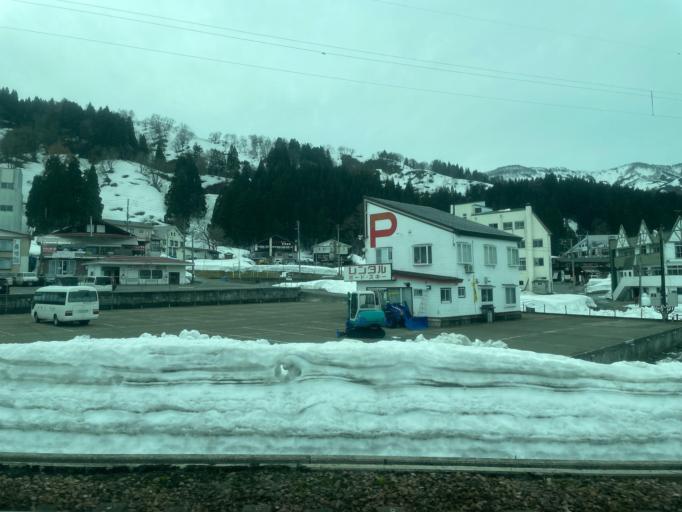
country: JP
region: Niigata
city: Shiozawa
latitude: 36.9817
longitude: 138.8006
